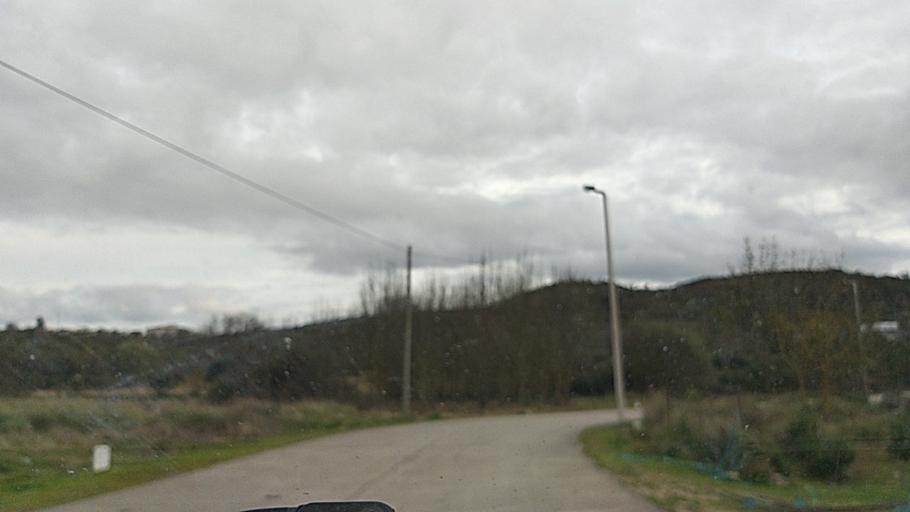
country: PT
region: Guarda
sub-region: Celorico da Beira
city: Celorico da Beira
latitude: 40.6324
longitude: -7.4135
